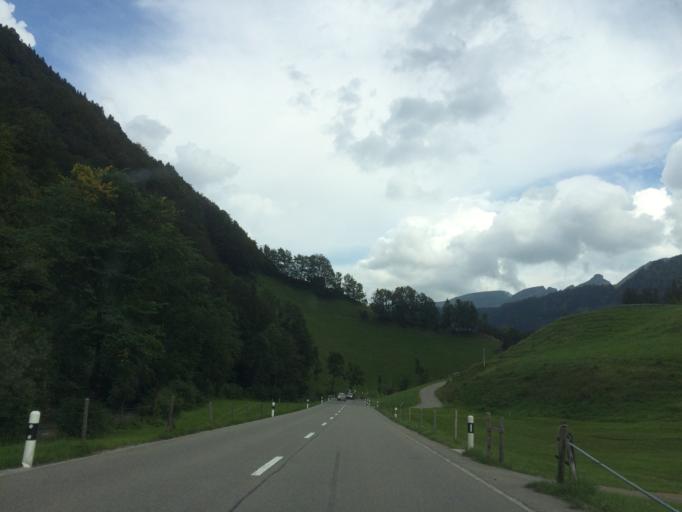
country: CH
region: Saint Gallen
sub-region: Wahlkreis Toggenburg
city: Krummenau
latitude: 47.1931
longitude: 9.2310
